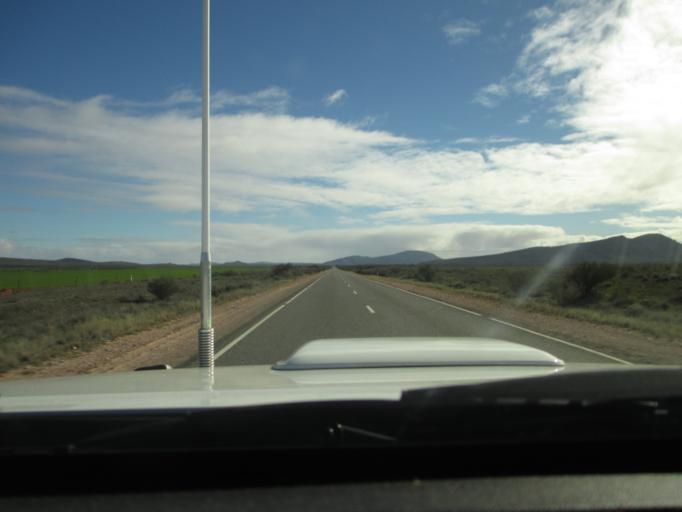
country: AU
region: South Australia
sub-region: Flinders Ranges
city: Quorn
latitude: -31.8715
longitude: 138.4090
